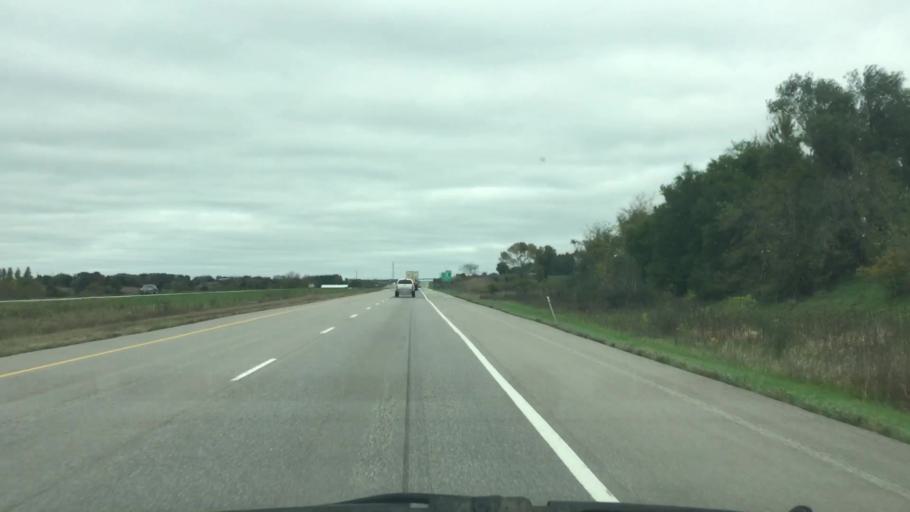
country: US
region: Iowa
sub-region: Warren County
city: Norwalk
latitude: 41.4585
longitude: -93.7798
